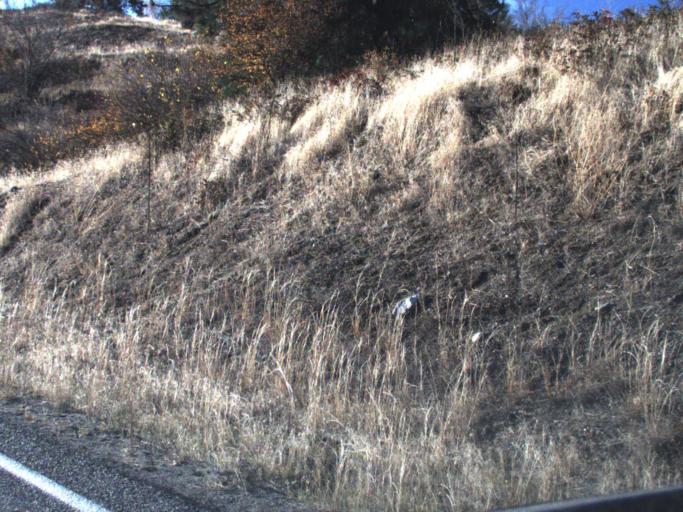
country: CA
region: British Columbia
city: Rossland
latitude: 48.8512
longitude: -117.8949
